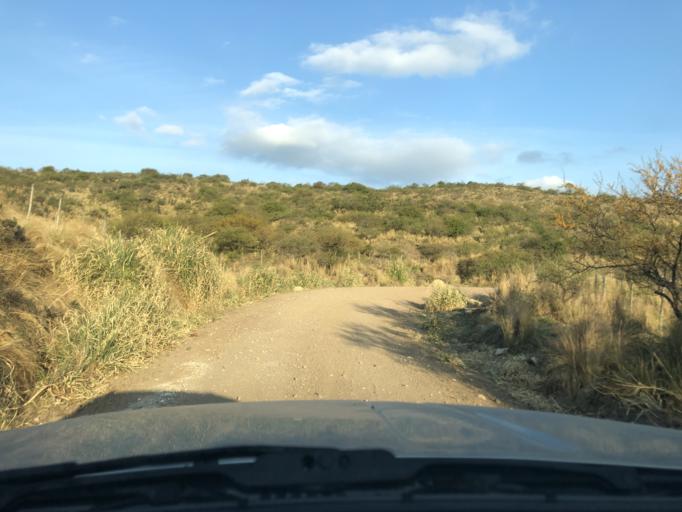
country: AR
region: Cordoba
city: Agua de Oro
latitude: -31.0556
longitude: -64.3526
